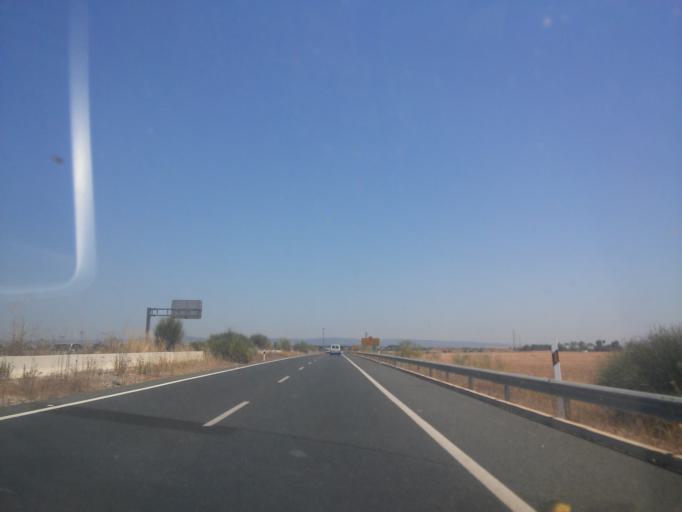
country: ES
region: Andalusia
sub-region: Provincia de Sevilla
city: La Rinconada
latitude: 37.4613
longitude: -5.9684
